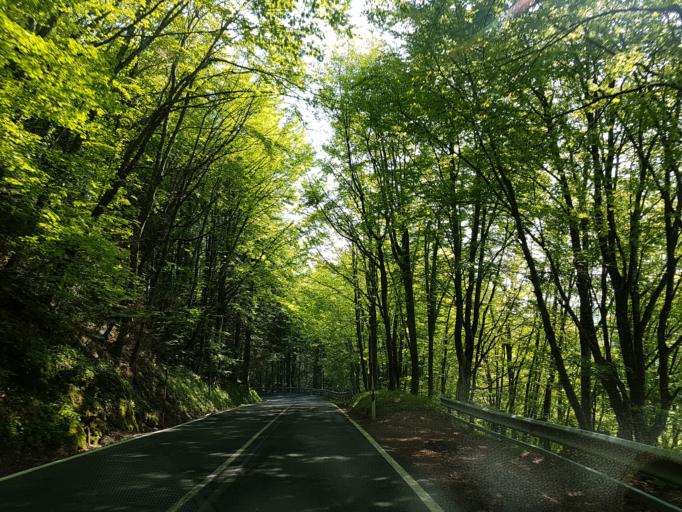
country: IT
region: Tuscany
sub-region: Province of Arezzo
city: Soci
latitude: 43.7949
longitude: 11.8923
